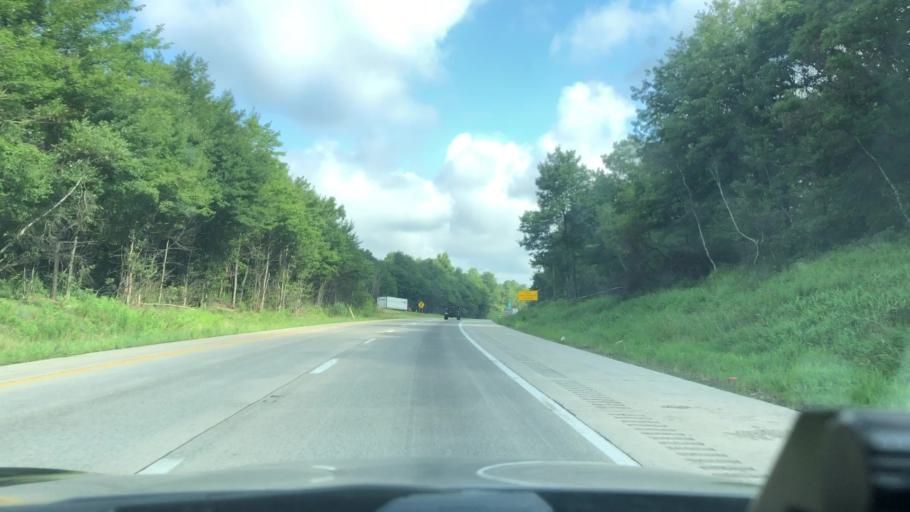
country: US
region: Pennsylvania
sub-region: Monroe County
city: Emerald Lakes
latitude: 41.0733
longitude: -75.3931
